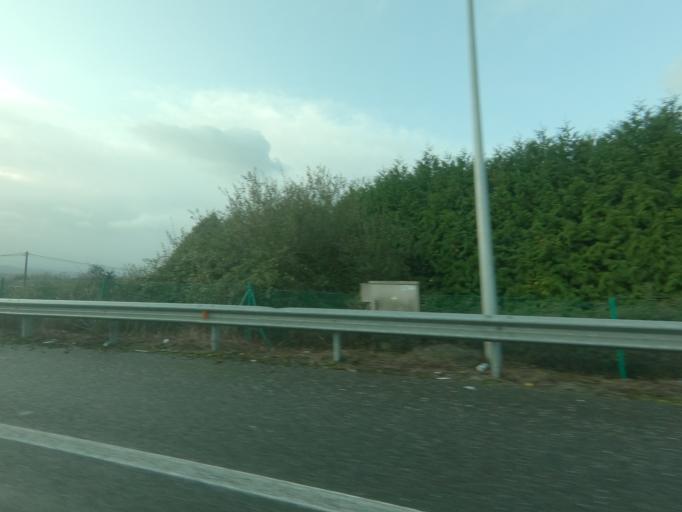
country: ES
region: Galicia
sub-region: Provincia de Pontevedra
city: Tui
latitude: 42.0666
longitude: -8.6408
